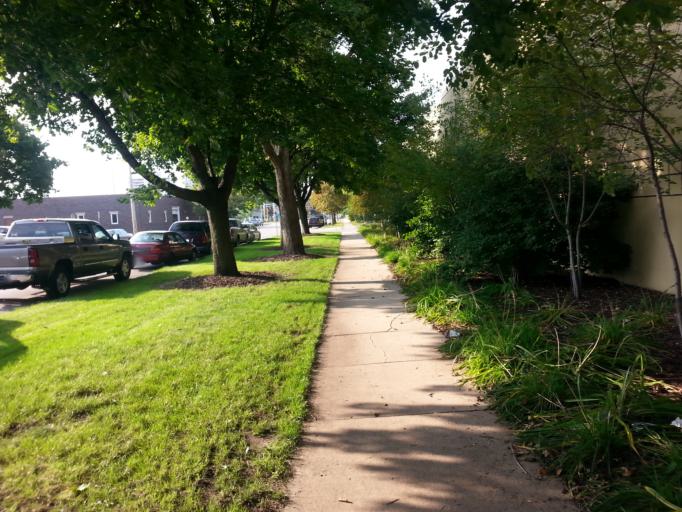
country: US
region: Minnesota
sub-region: Olmsted County
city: Rochester
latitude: 44.0287
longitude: -92.4646
